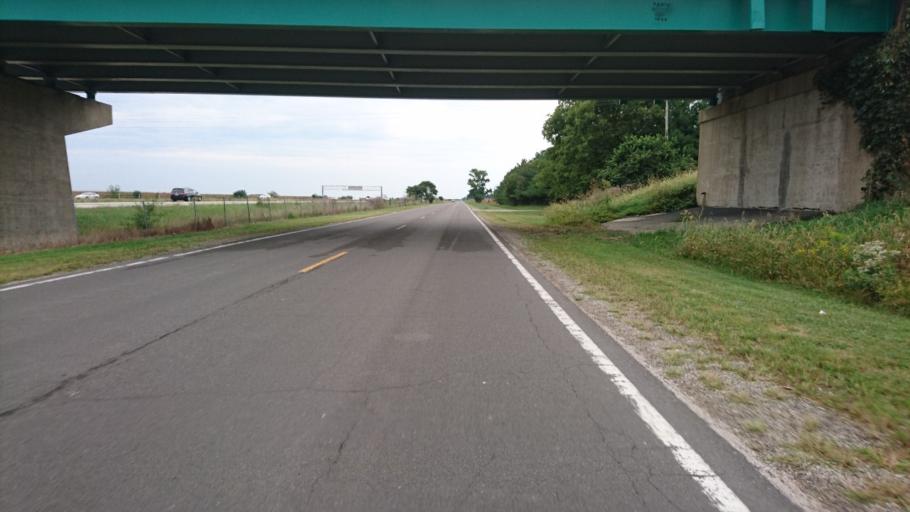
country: US
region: Illinois
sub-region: Sangamon County
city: Chatham
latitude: 39.6702
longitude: -89.6482
